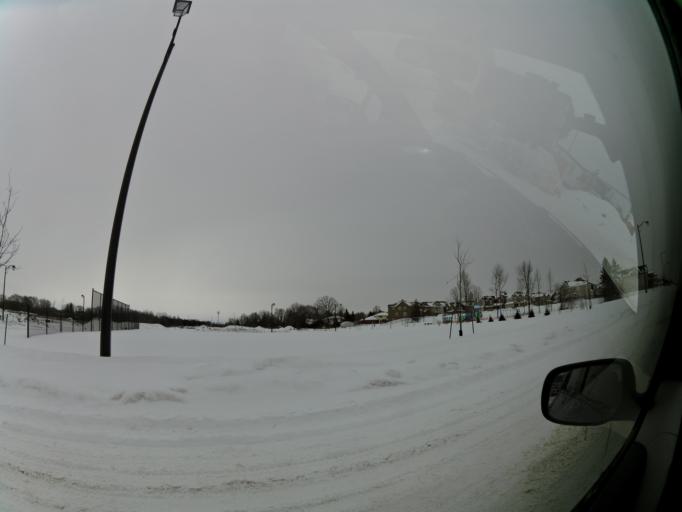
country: CA
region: Ontario
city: Bells Corners
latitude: 45.2833
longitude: -75.9226
